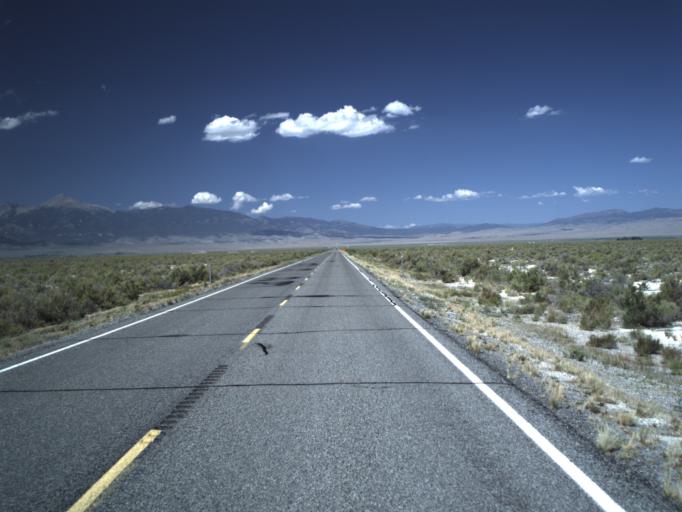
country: US
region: Nevada
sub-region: White Pine County
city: McGill
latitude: 39.0472
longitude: -113.9195
